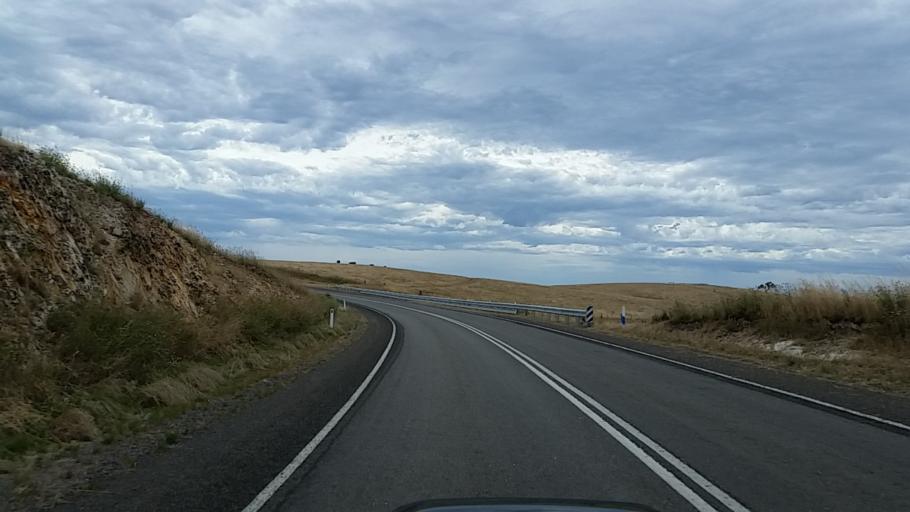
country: AU
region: South Australia
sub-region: Onkaparinga
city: Port Willunga
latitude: -35.3774
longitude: 138.4438
